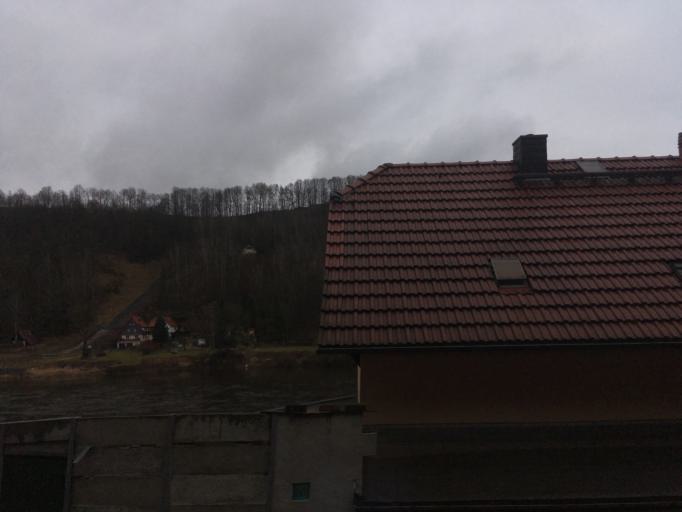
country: DE
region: Saxony
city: Struppen
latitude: 50.9473
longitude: 13.9949
